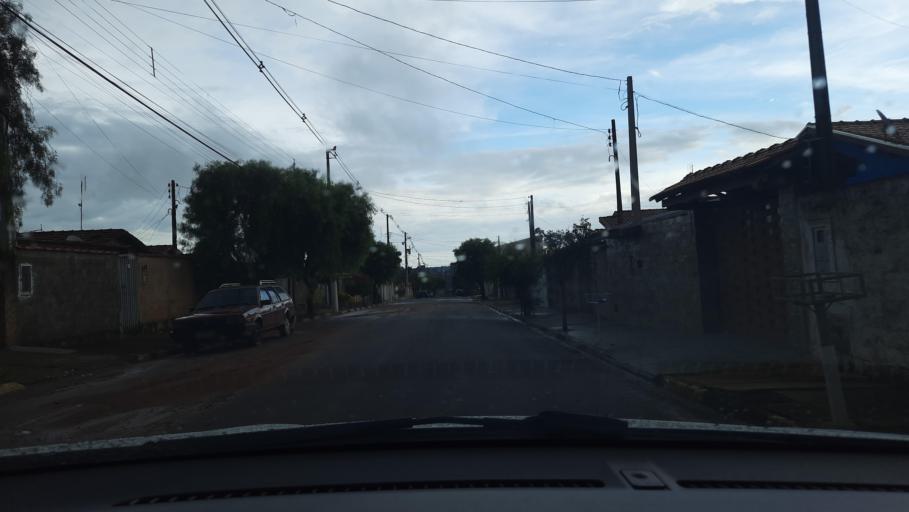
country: BR
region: Sao Paulo
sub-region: Casa Branca
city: Casa Branca
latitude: -21.7592
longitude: -47.0770
